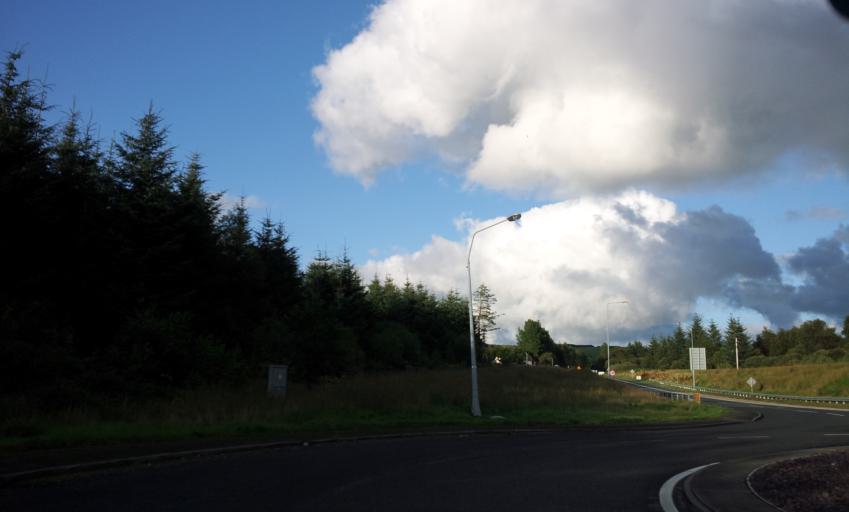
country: IE
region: Munster
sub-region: Ciarrai
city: Castleisland
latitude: 52.2605
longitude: -9.4633
